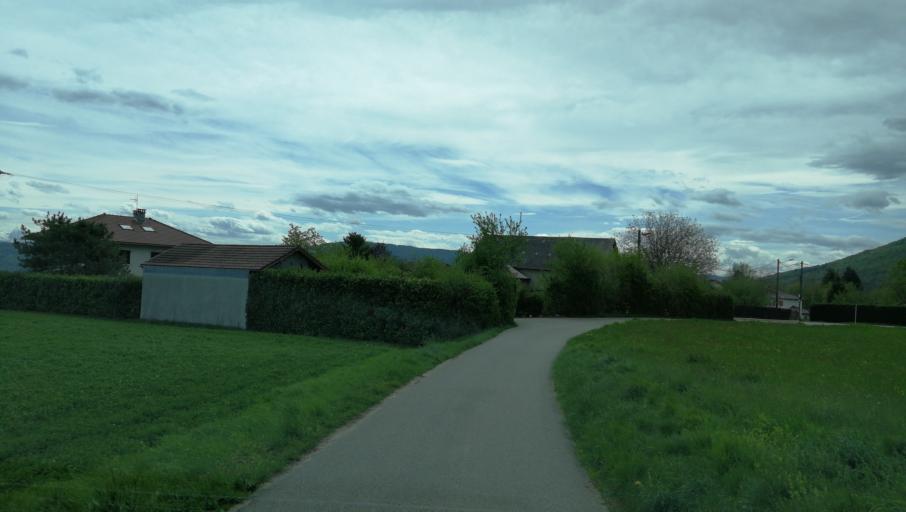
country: FR
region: Rhone-Alpes
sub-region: Departement de l'Ain
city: Bellegarde-sur-Valserine
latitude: 46.0086
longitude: 5.7824
